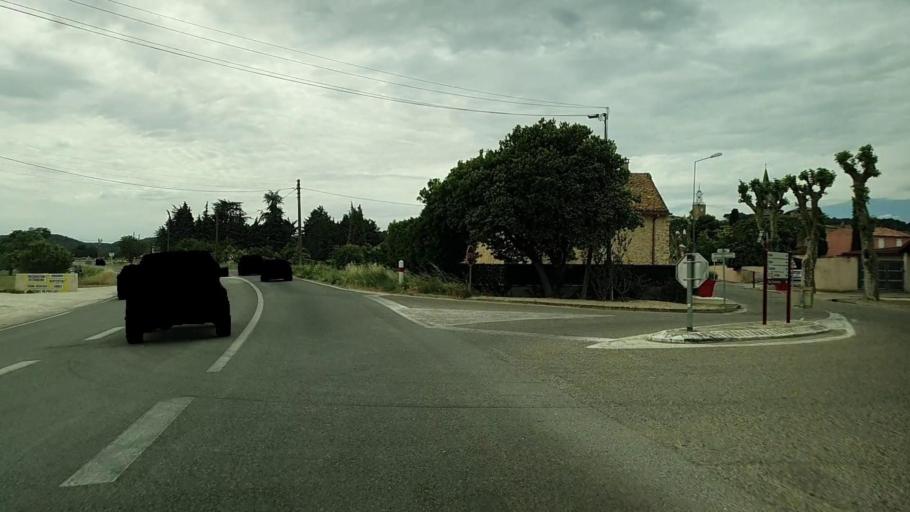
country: FR
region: Languedoc-Roussillon
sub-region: Departement du Gard
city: Connaux
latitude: 44.0942
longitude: 4.5970
